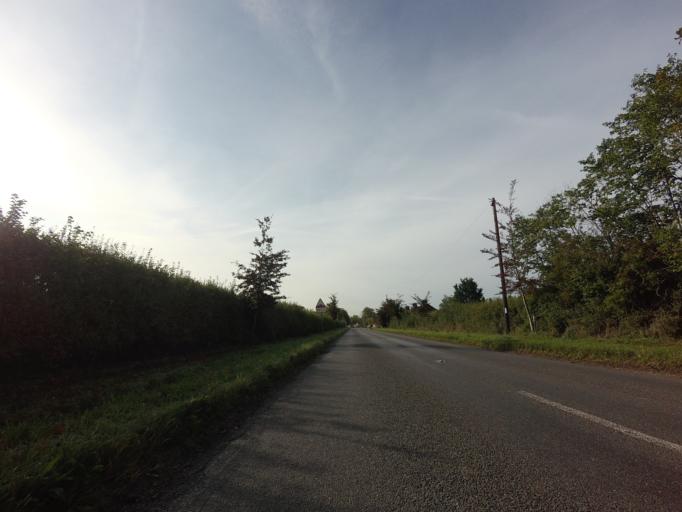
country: GB
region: England
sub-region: Cambridgeshire
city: Harston
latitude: 52.1276
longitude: 0.0998
